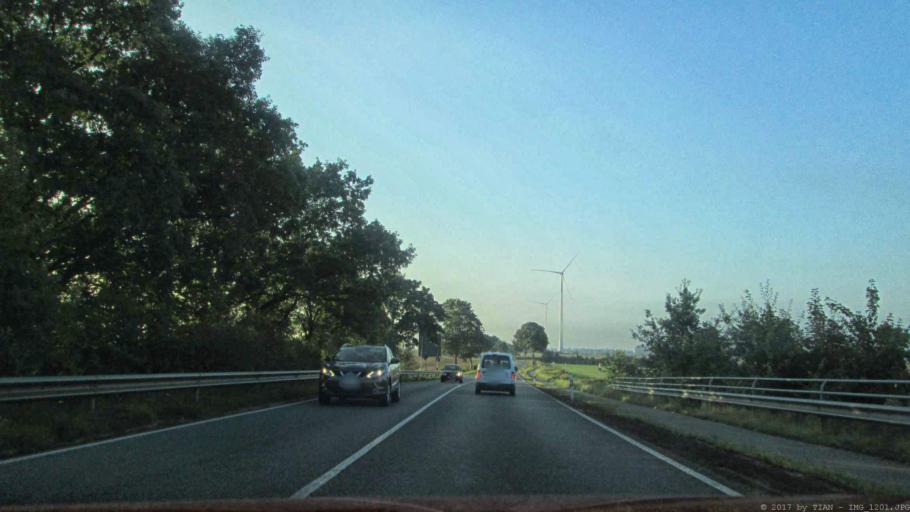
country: DE
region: Lower Saxony
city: Uelzen
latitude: 52.9475
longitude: 10.5866
